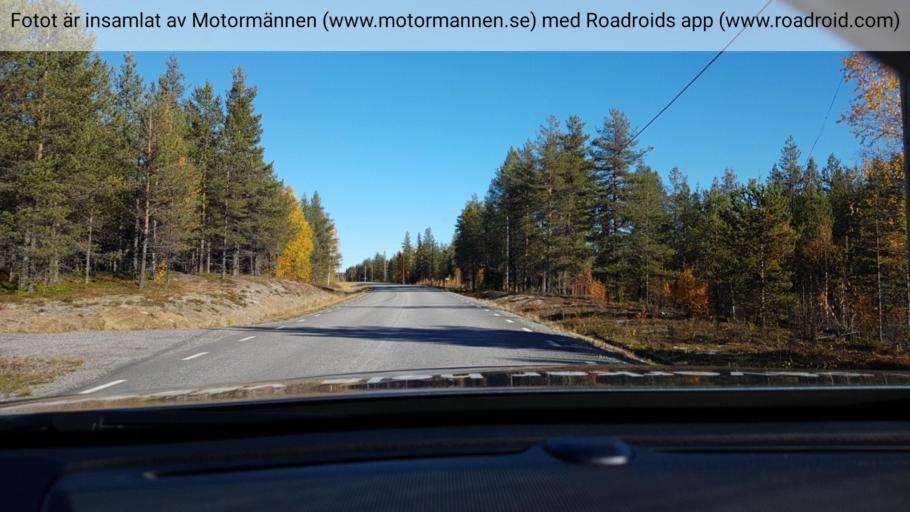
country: SE
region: Norrbotten
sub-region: Gallivare Kommun
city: Gaellivare
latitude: 66.7541
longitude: 21.0069
